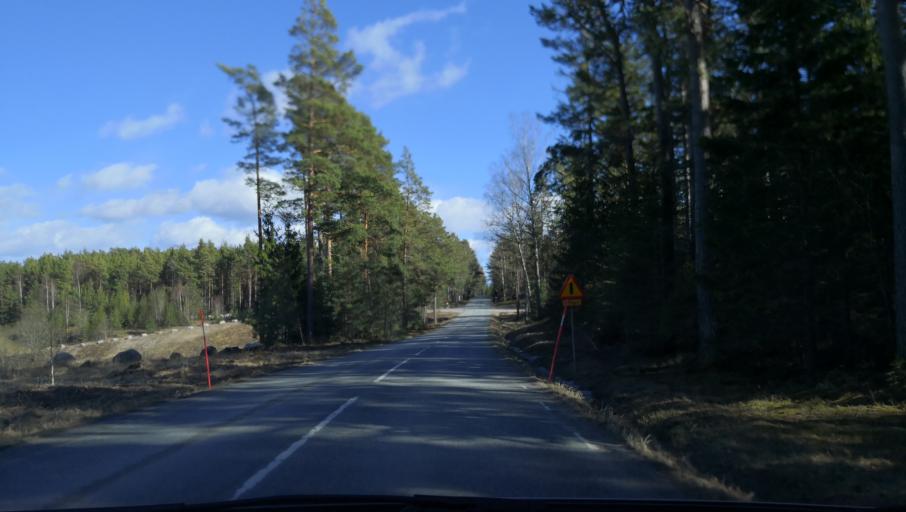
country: SE
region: Stockholm
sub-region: Varmdo Kommun
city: Hemmesta
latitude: 59.3574
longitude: 18.5887
